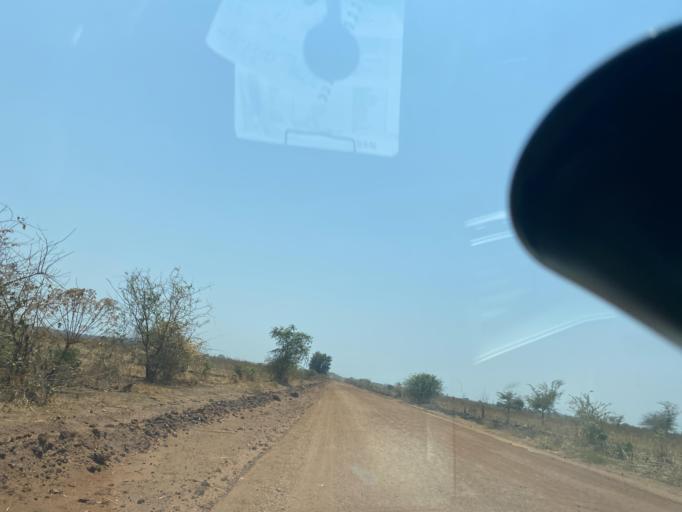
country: ZM
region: Lusaka
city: Lusaka
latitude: -15.4636
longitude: 27.9108
